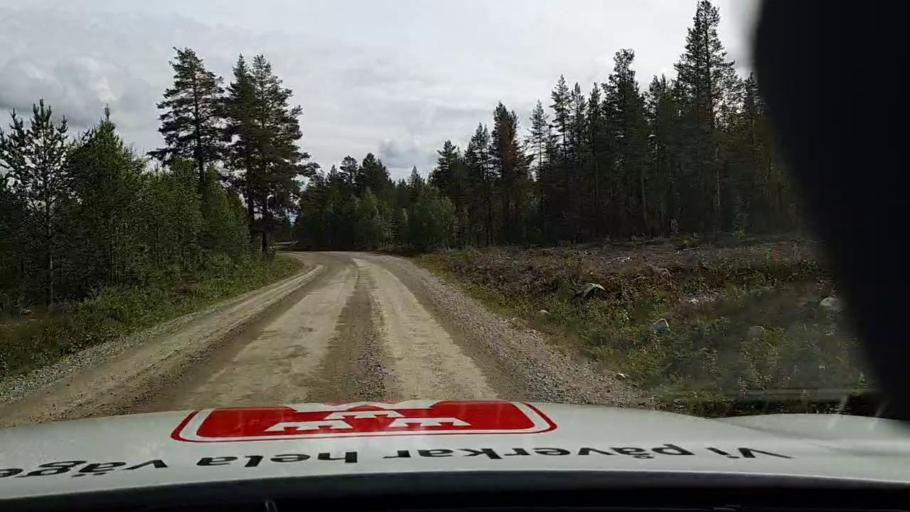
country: SE
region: Jaemtland
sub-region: Are Kommun
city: Jarpen
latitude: 62.5054
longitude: 13.4985
